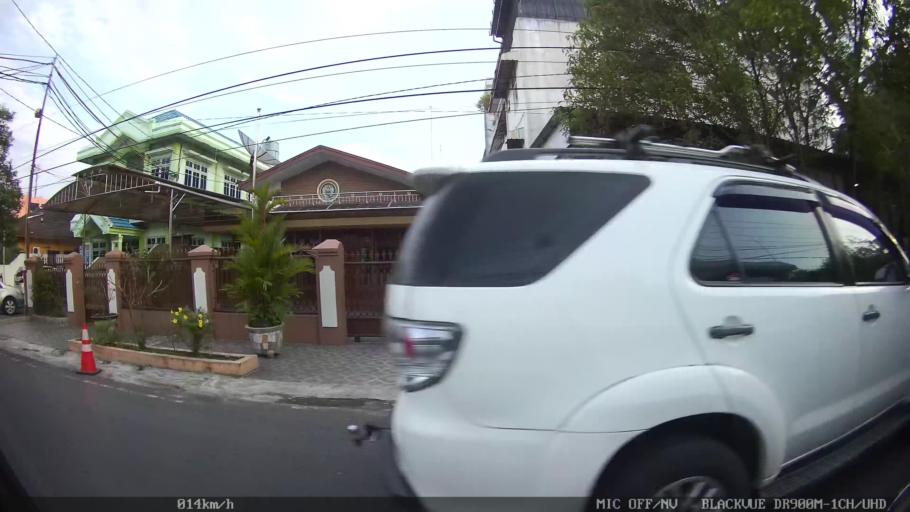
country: ID
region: North Sumatra
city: Medan
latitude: 3.5767
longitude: 98.6612
